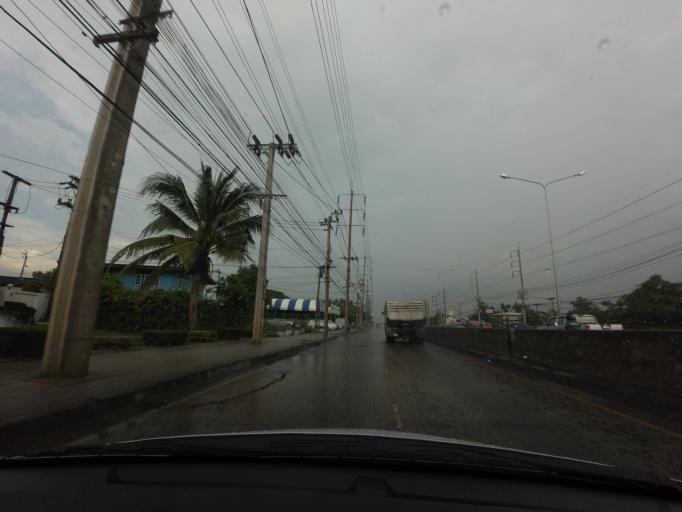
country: TH
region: Bangkok
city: Min Buri
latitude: 13.8151
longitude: 100.7552
